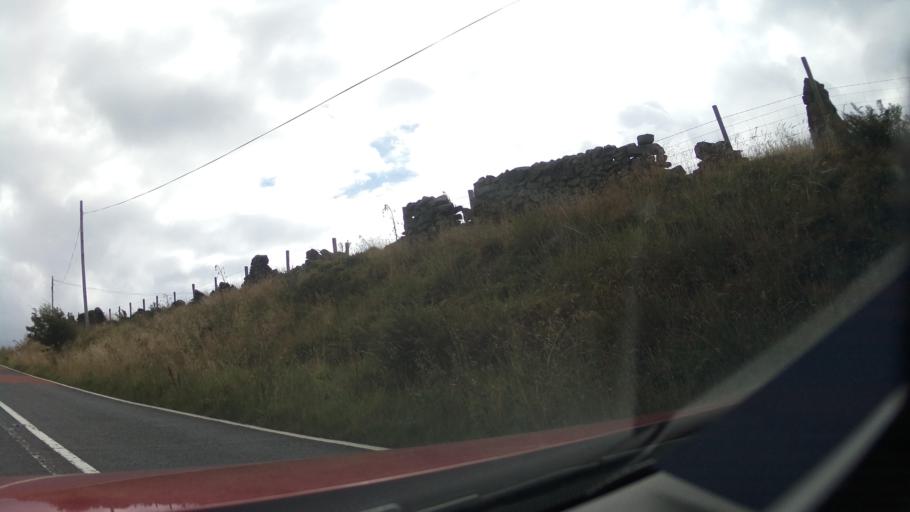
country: GB
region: England
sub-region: Kirklees
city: Meltham
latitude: 53.5434
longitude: -1.8457
